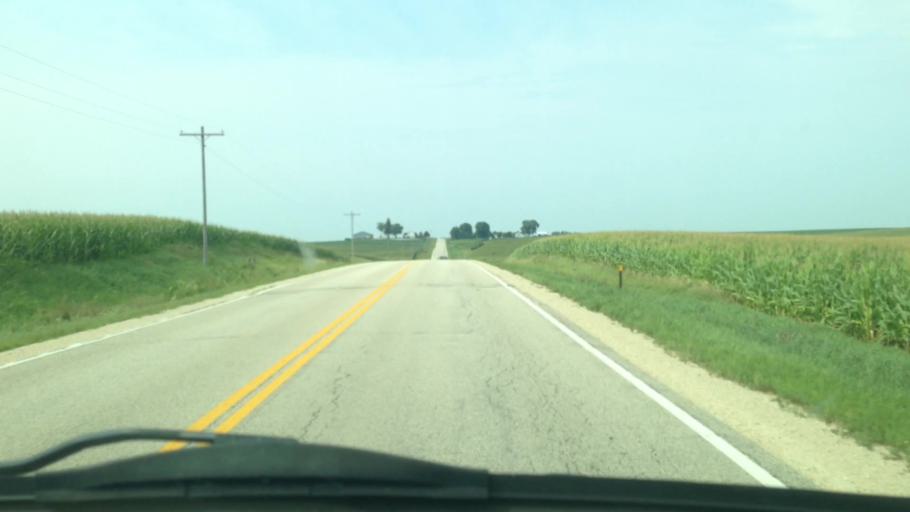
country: US
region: Minnesota
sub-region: Winona County
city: Lewiston
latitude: 43.8841
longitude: -91.9594
